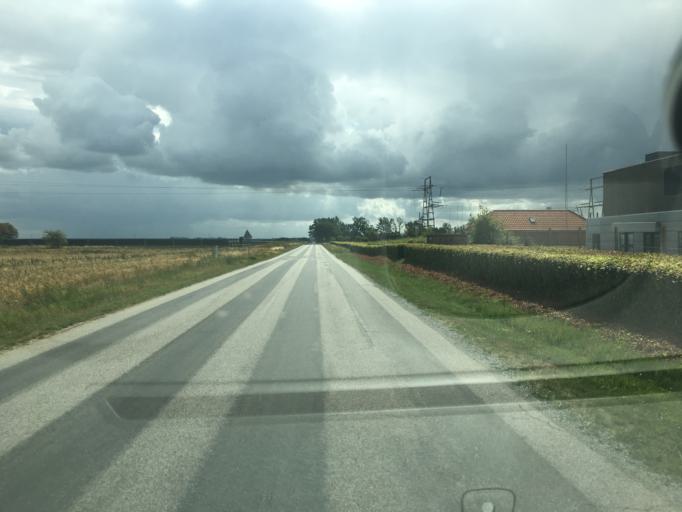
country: DK
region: South Denmark
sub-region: Tonder Kommune
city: Logumkloster
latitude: 55.0526
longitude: 8.9583
